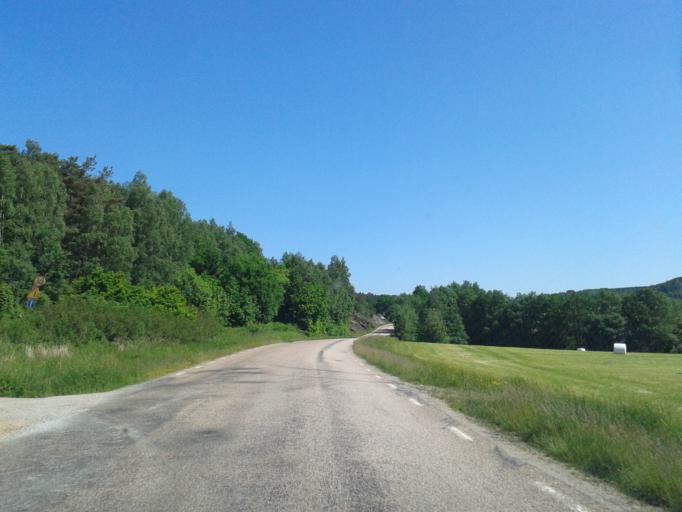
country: SE
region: Vaestra Goetaland
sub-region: Orust
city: Henan
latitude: 58.2543
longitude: 11.7232
